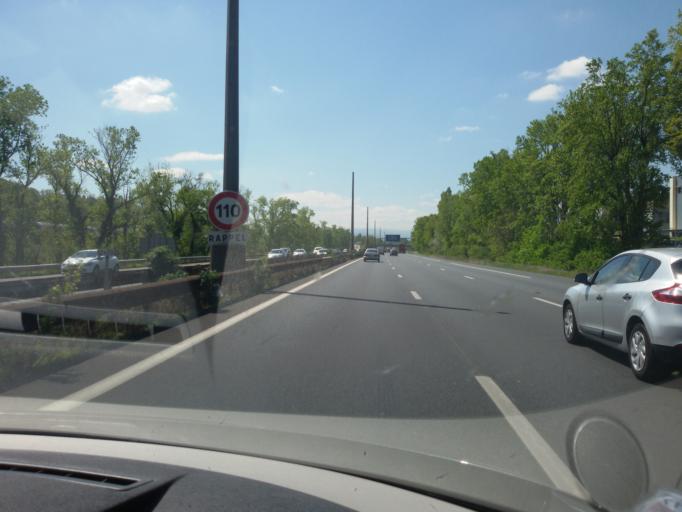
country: FR
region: Rhone-Alpes
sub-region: Departement du Rhone
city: Serezin-du-Rhone
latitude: 45.6470
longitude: 4.8325
